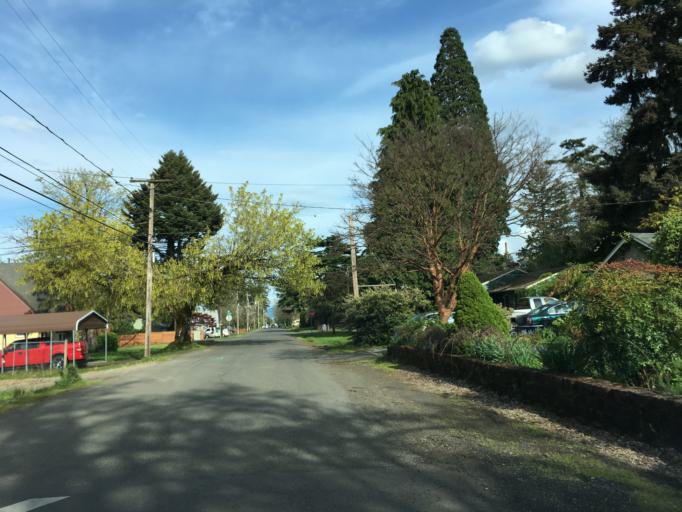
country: US
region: Oregon
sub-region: Multnomah County
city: Lents
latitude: 45.5499
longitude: -122.5558
